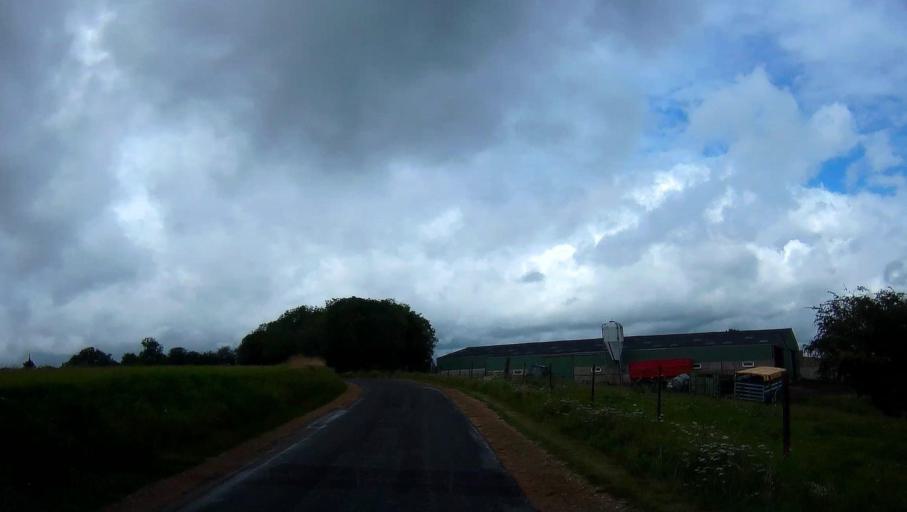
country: FR
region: Champagne-Ardenne
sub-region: Departement des Ardennes
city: Rimogne
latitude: 49.7605
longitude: 4.5146
